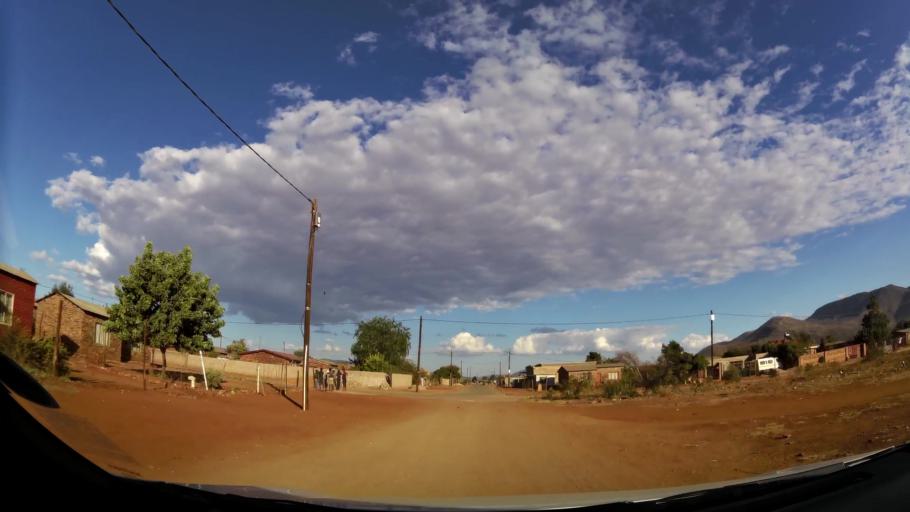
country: ZA
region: Limpopo
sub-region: Waterberg District Municipality
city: Mokopane
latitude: -24.1837
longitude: 28.9716
